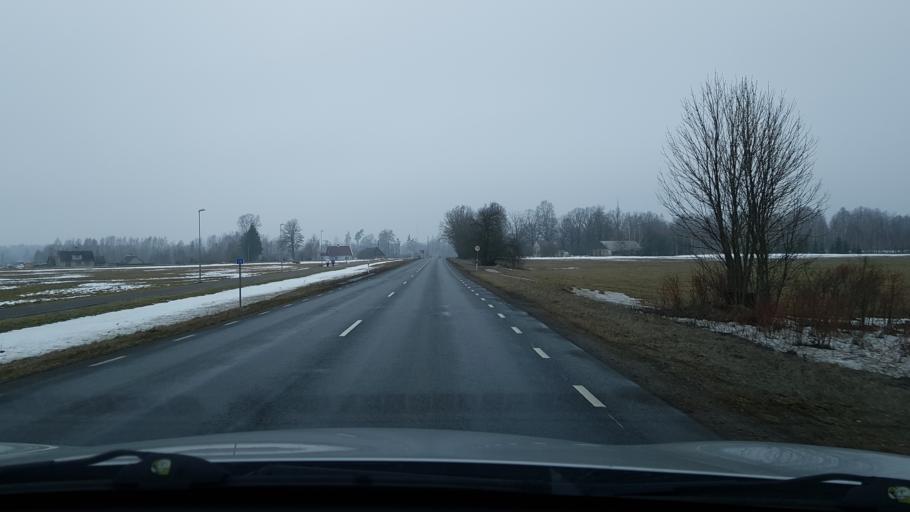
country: EE
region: Valgamaa
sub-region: Torva linn
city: Torva
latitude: 58.2239
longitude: 25.8922
